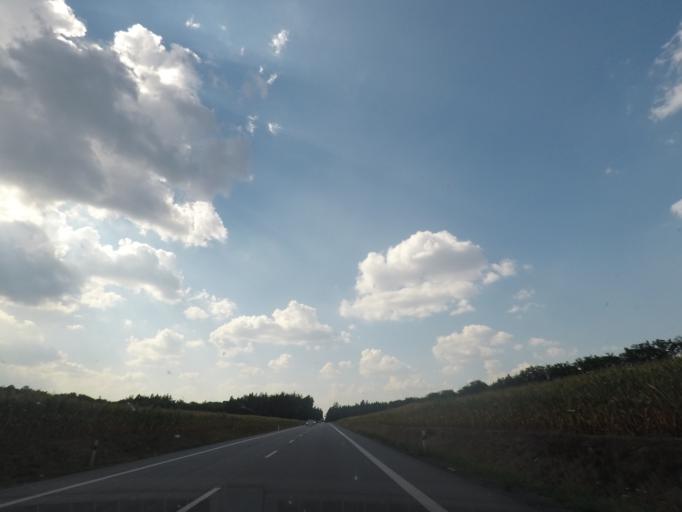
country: CZ
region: Kralovehradecky
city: Trebechovice pod Orebem
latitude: 50.1786
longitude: 16.0254
